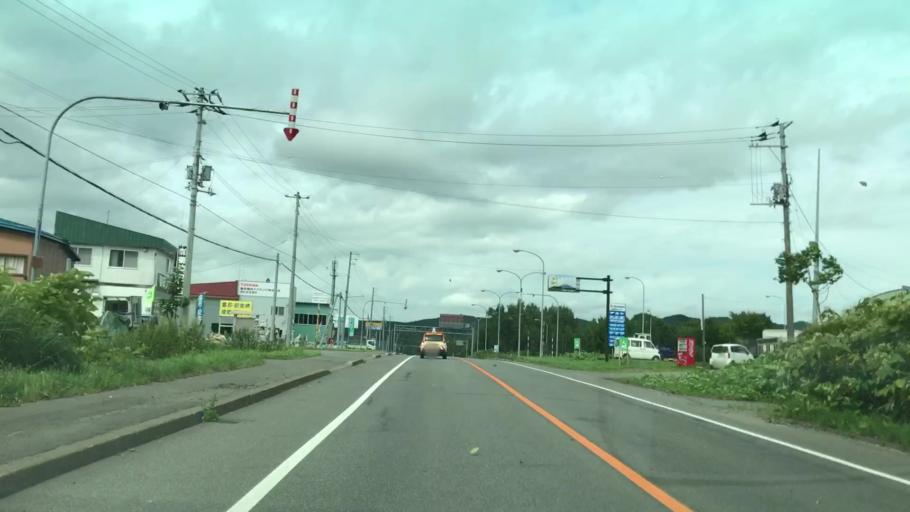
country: JP
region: Hokkaido
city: Niseko Town
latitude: 42.9142
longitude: 140.7507
